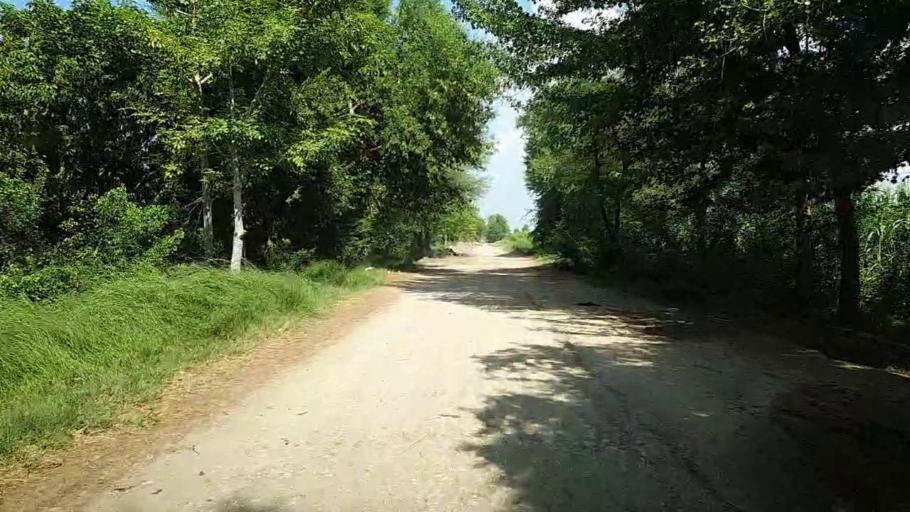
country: PK
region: Sindh
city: Bhiria
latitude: 26.9174
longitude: 68.2386
